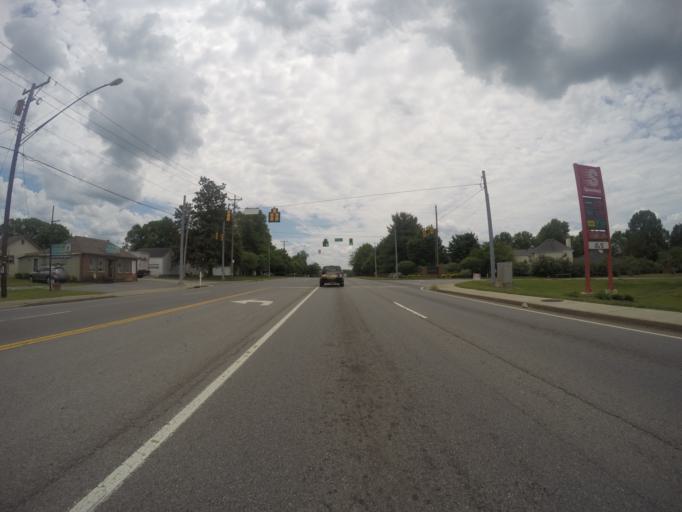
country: US
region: Tennessee
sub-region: Davidson County
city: Lakewood
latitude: 36.2170
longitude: -86.6236
